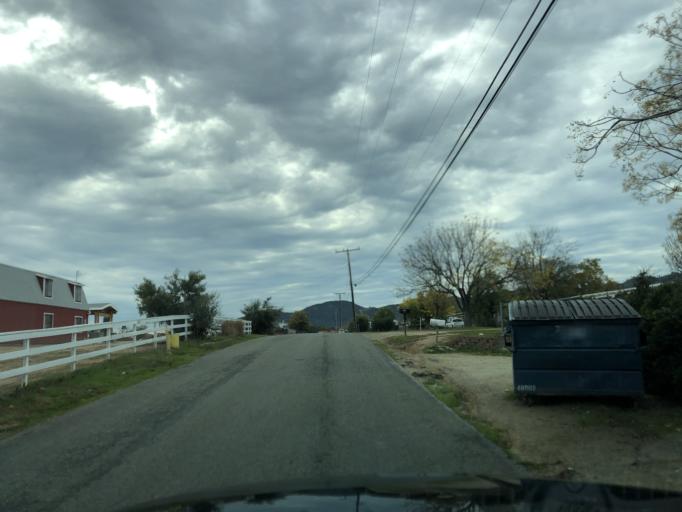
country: US
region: California
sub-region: Riverside County
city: Sedco Hills
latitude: 33.6222
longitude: -117.2842
